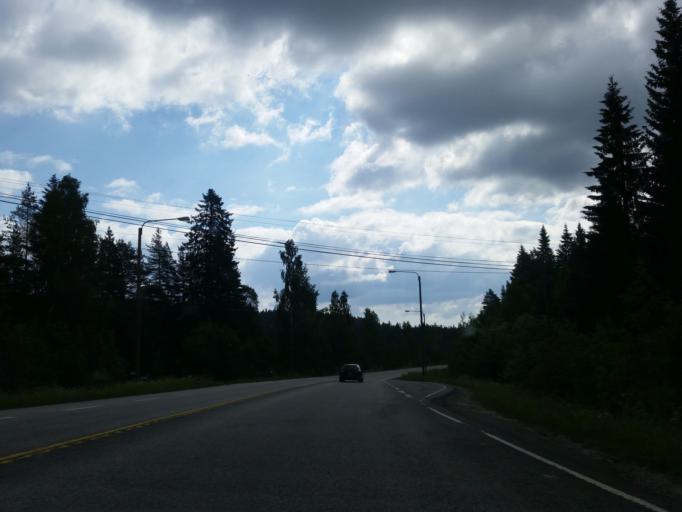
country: FI
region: Northern Savo
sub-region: Kuopio
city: Kuopio
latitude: 62.8497
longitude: 27.5408
